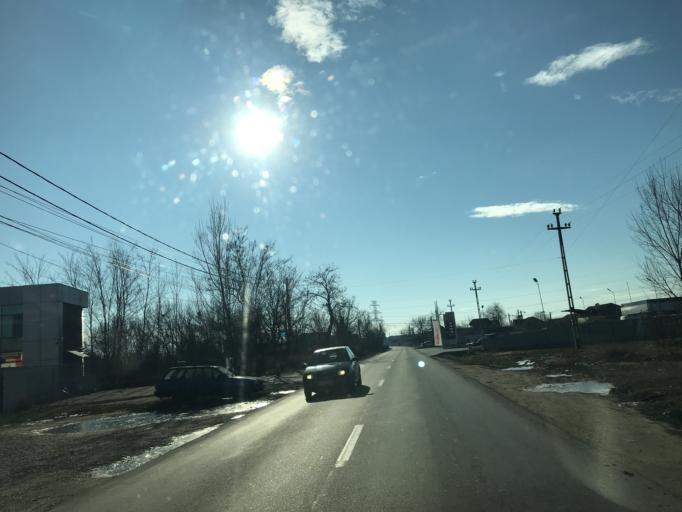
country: RO
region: Olt
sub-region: Comuna Slatioara
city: Slatioara
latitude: 44.4157
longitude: 24.3267
